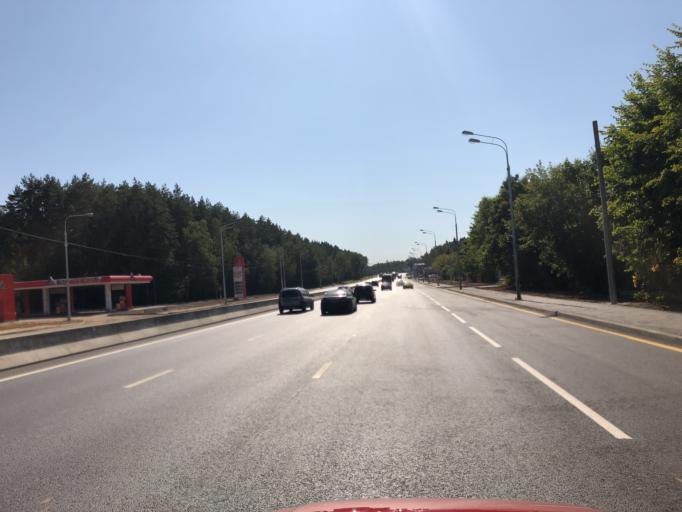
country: RU
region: Moskovskaya
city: Troitsk
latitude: 55.4723
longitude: 37.3094
